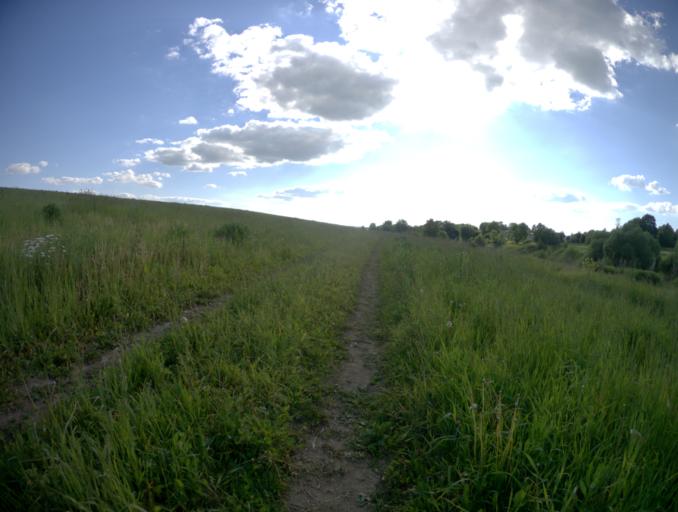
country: RU
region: Vladimir
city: Stavrovo
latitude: 56.2610
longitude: 40.1824
